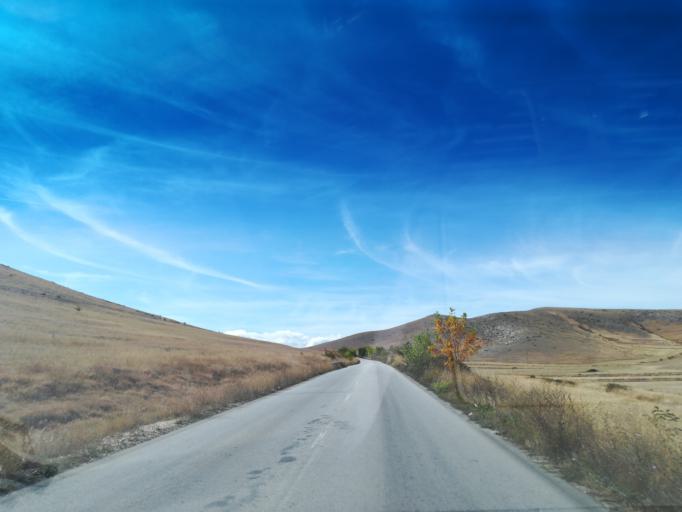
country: BG
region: Plovdiv
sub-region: Obshtina Krichim
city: Krichim
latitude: 42.1020
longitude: 24.4739
